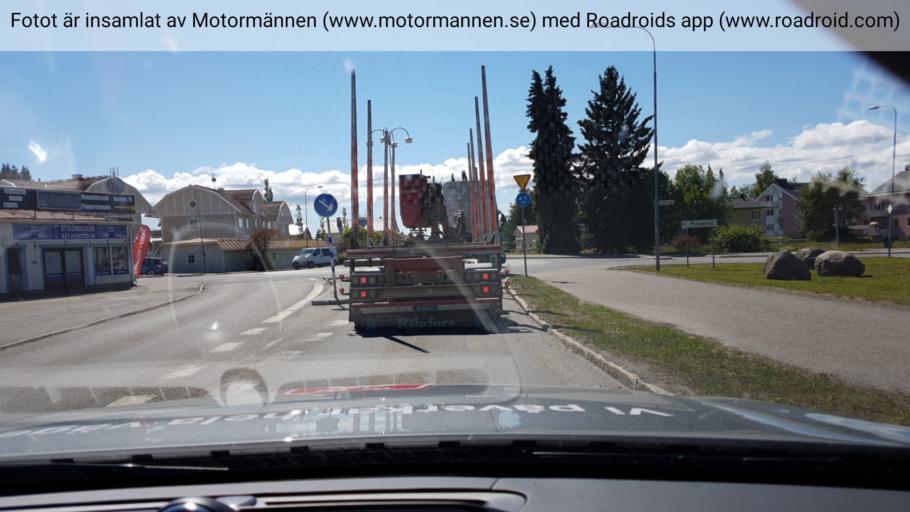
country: SE
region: Jaemtland
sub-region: Stroemsunds Kommun
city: Stroemsund
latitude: 63.8545
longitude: 15.5607
